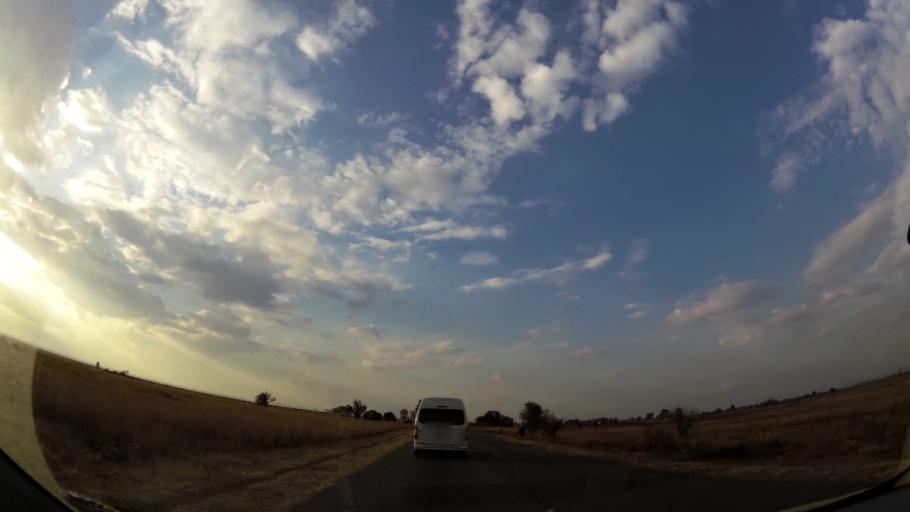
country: ZA
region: Gauteng
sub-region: Sedibeng District Municipality
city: Vanderbijlpark
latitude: -26.6265
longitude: 27.8102
